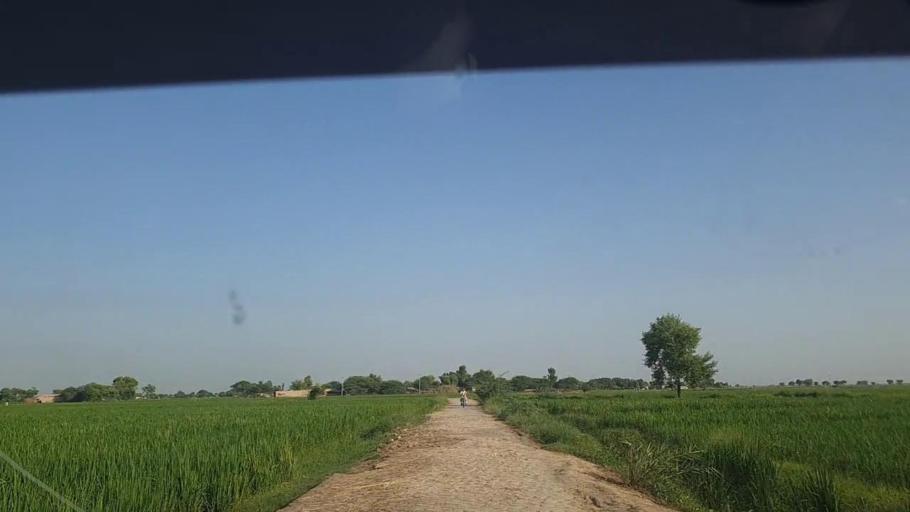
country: PK
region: Sindh
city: Tangwani
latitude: 28.2690
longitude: 69.0109
